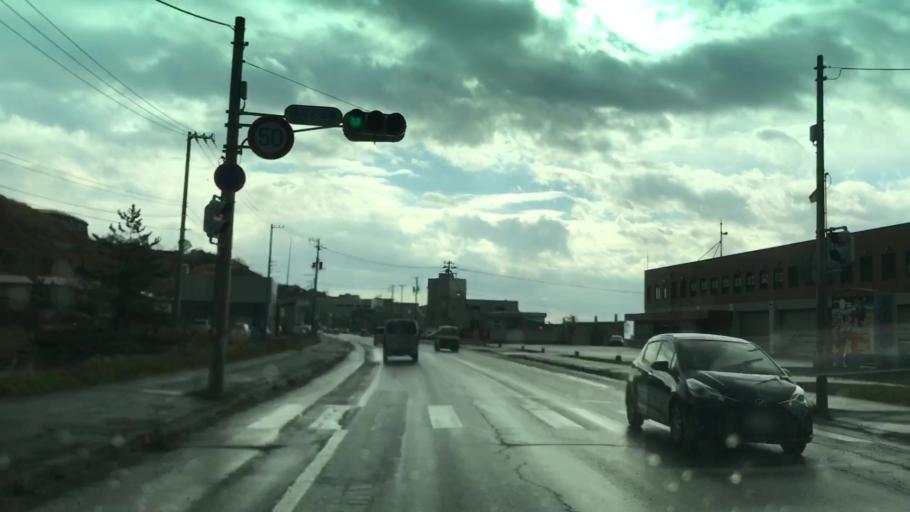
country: JP
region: Hokkaido
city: Shizunai-furukawacho
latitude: 42.1683
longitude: 142.7695
